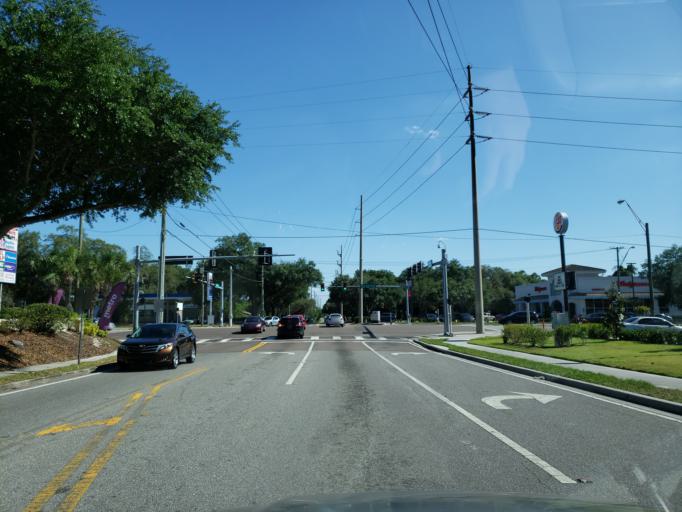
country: US
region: Florida
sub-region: Hillsborough County
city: Mango
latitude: 27.9821
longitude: -82.3105
